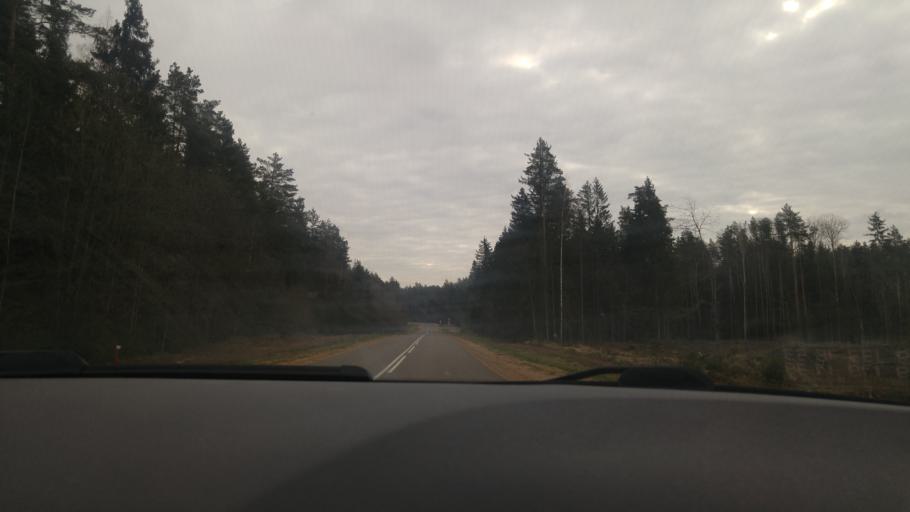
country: BY
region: Minsk
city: Chervyen'
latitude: 53.7344
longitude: 28.2996
